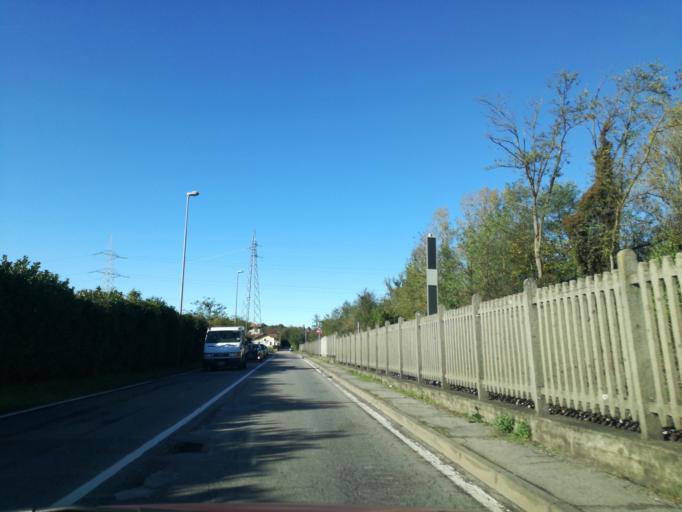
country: IT
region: Lombardy
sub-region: Provincia di Monza e Brianza
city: Lesmo
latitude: 45.6362
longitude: 9.2945
